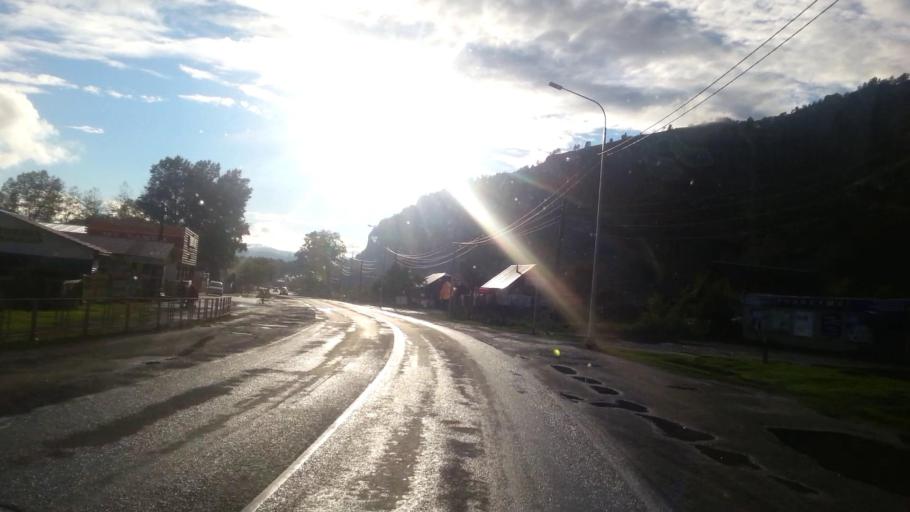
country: RU
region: Altay
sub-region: Mayminskiy Rayon
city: Manzherok
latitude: 51.8337
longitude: 85.7800
